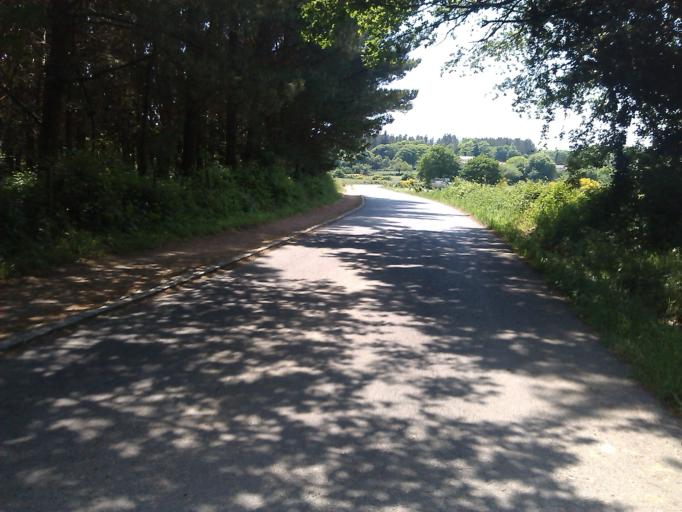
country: ES
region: Galicia
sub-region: Provincia de Lugo
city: Monterroso
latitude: 42.8732
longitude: -7.8102
